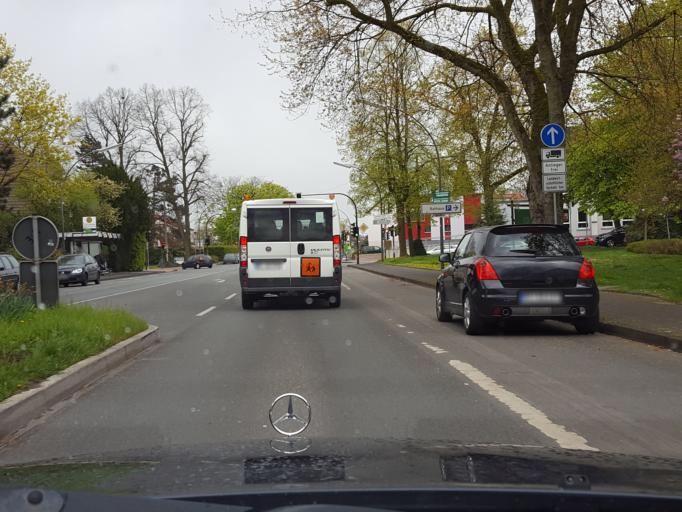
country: DE
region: North Rhine-Westphalia
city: Waltrop
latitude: 51.6235
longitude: 7.3902
